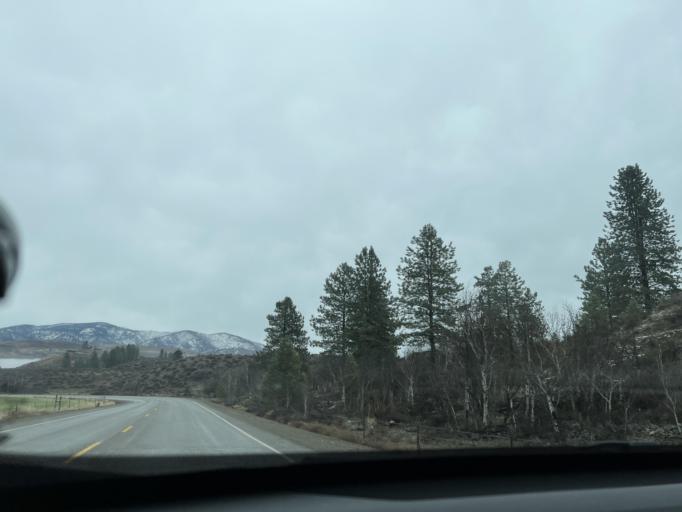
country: US
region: Washington
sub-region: Okanogan County
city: Brewster
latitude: 48.4695
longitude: -120.2019
